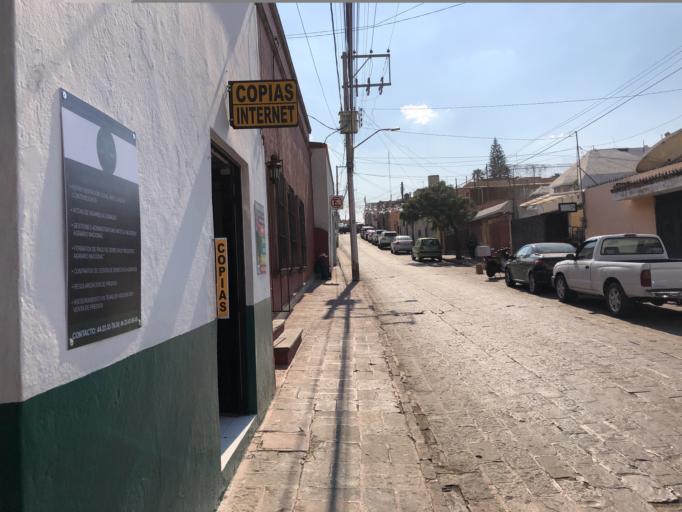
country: MX
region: Queretaro
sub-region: Queretaro
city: Santiago de Queretaro
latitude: 20.5966
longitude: -100.3819
